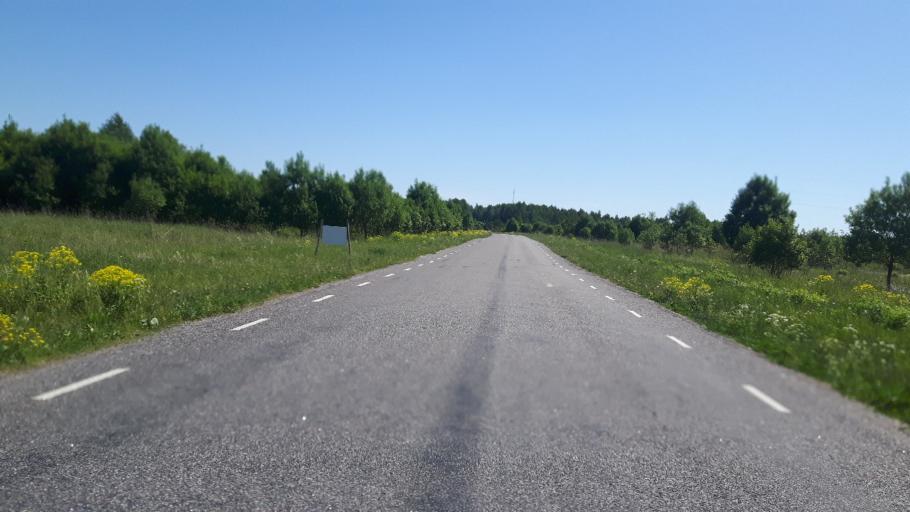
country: EE
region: Raplamaa
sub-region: Kohila vald
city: Kohila
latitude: 59.1859
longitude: 24.7136
